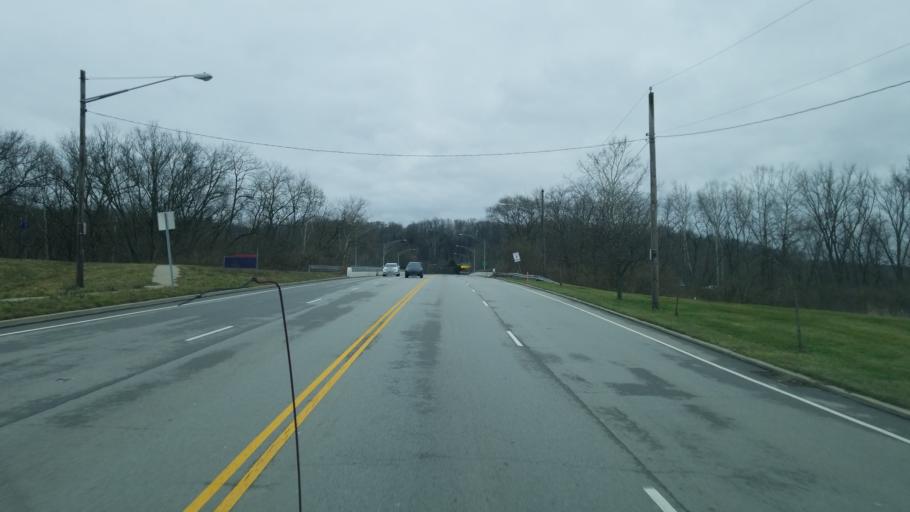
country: US
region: Kentucky
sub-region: Campbell County
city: Fort Thomas
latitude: 39.0871
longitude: -84.4224
